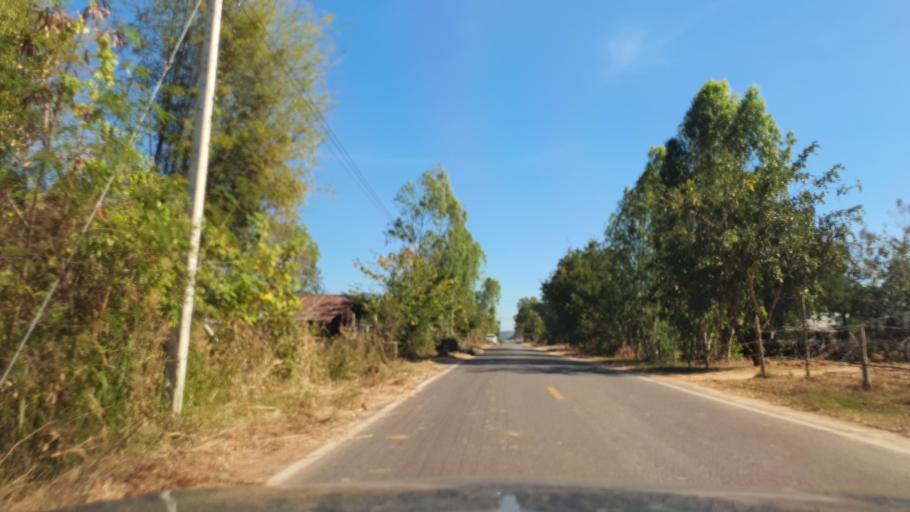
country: TH
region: Kalasin
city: Khao Wong
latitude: 16.7260
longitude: 104.1008
